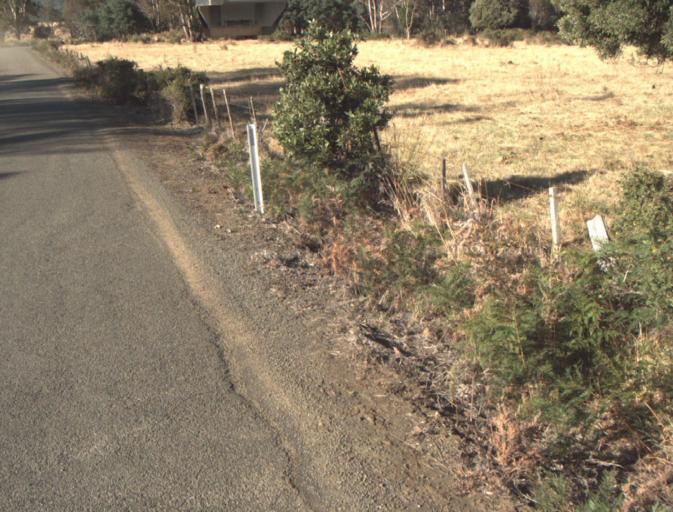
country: AU
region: Tasmania
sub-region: Launceston
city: Newstead
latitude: -41.4126
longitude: 147.2871
